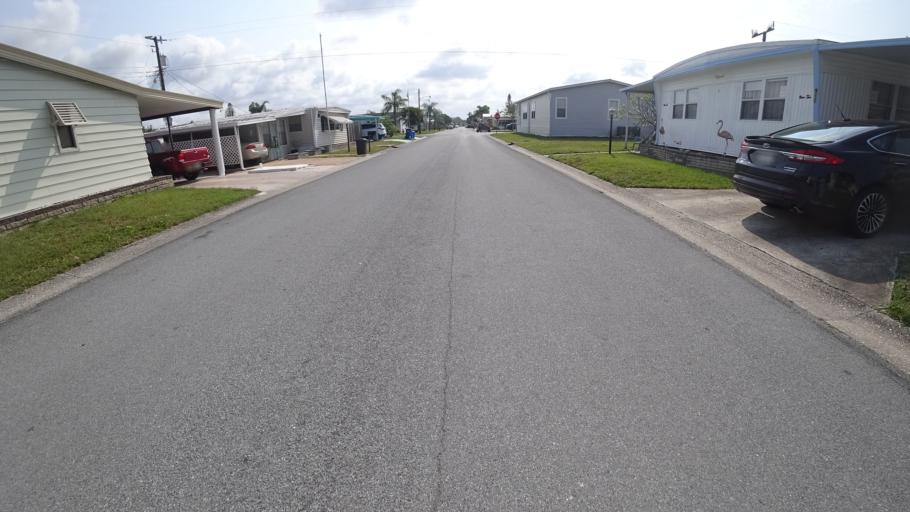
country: US
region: Florida
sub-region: Manatee County
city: South Bradenton
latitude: 27.4540
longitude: -82.5715
